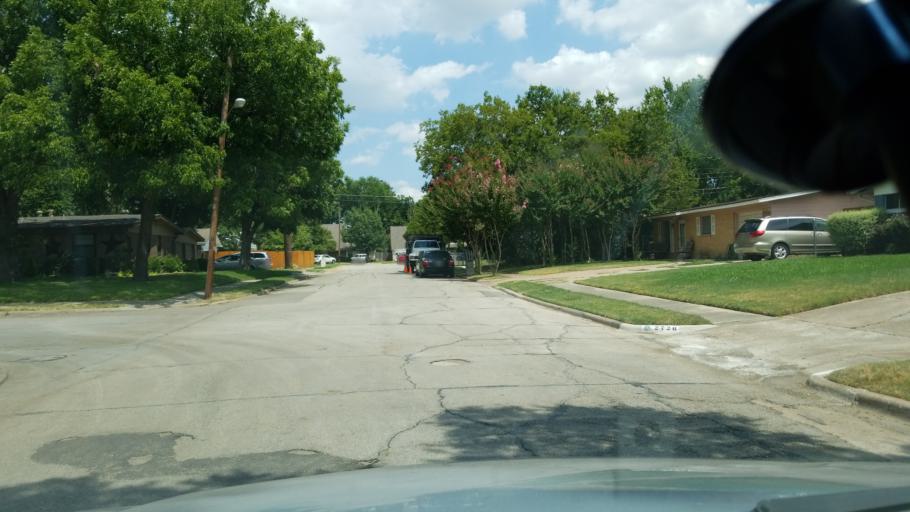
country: US
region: Texas
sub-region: Dallas County
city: Irving
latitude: 32.8232
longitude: -96.9827
